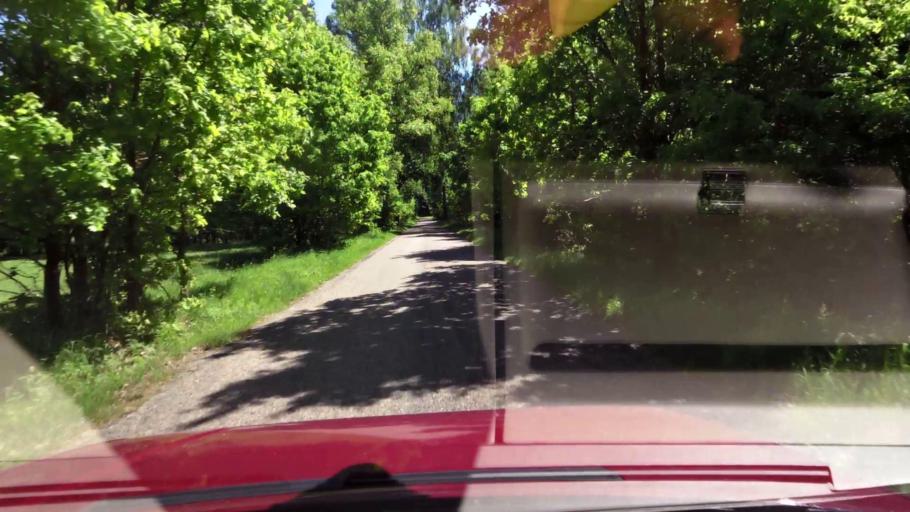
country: PL
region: West Pomeranian Voivodeship
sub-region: Powiat koszalinski
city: Bobolice
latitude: 54.0292
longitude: 16.6356
